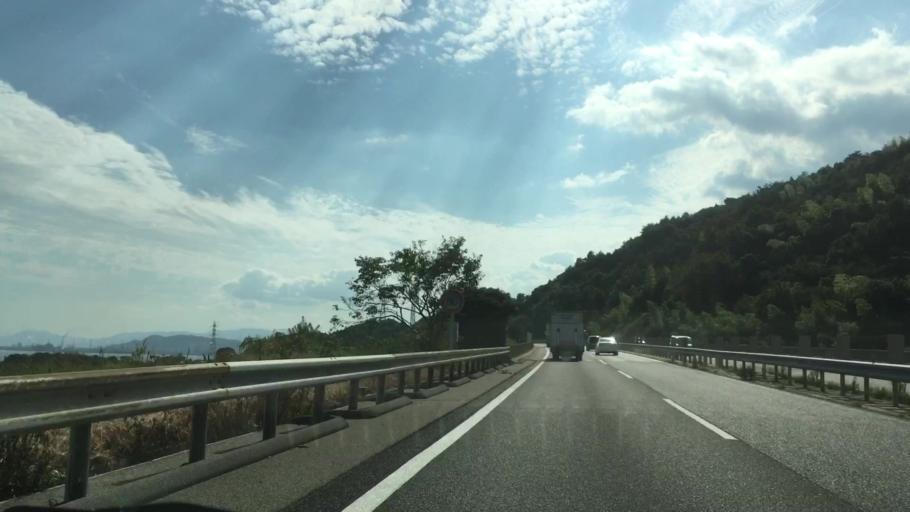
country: JP
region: Hiroshima
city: Ono-hara
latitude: 34.2855
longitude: 132.2628
